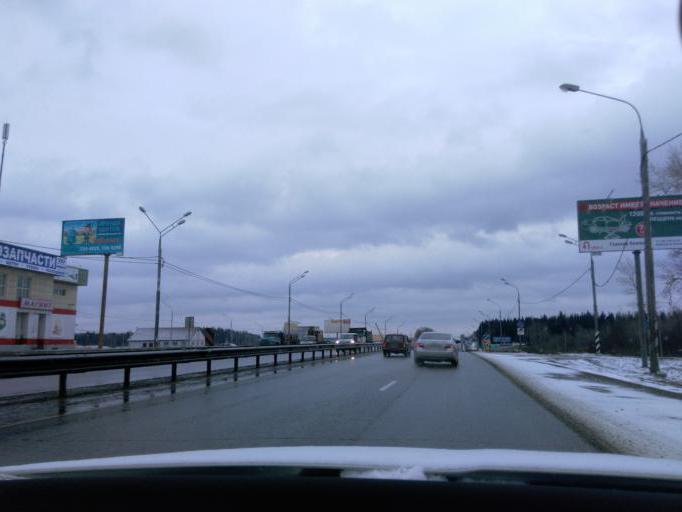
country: RU
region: Moskovskaya
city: Rzhavki
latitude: 55.9955
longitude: 37.2554
